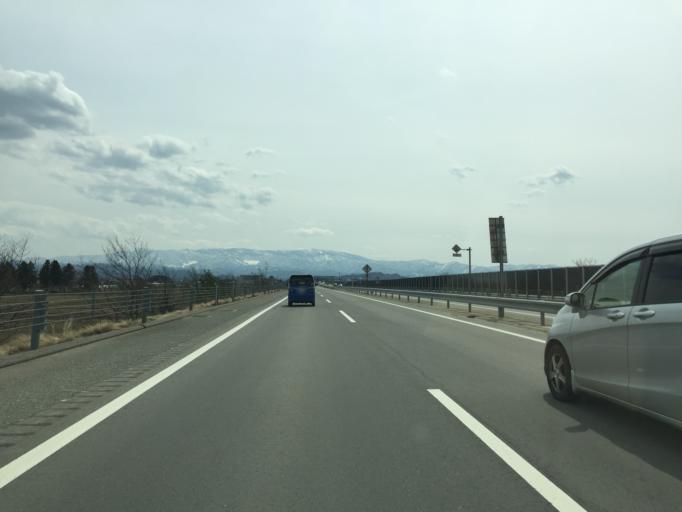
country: JP
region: Yamagata
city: Takahata
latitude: 38.0045
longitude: 140.1567
